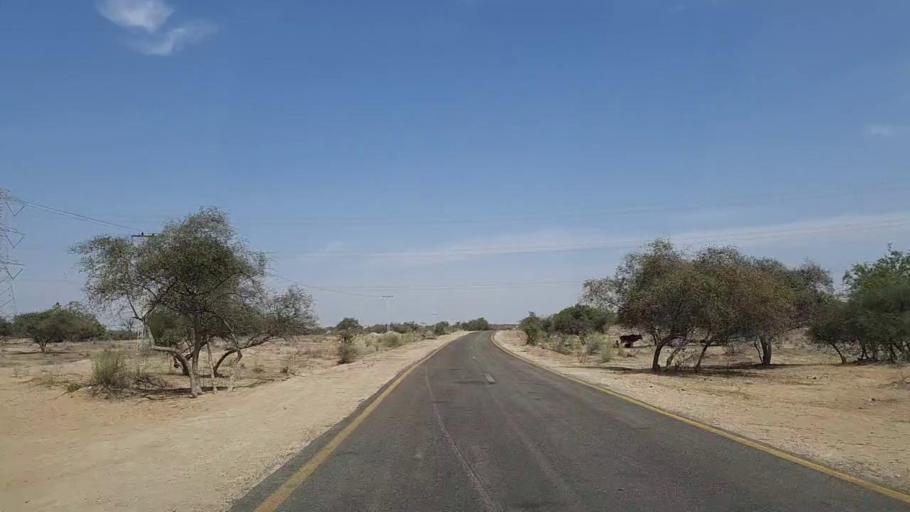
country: PK
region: Sindh
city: Mithi
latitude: 24.8507
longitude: 69.8378
